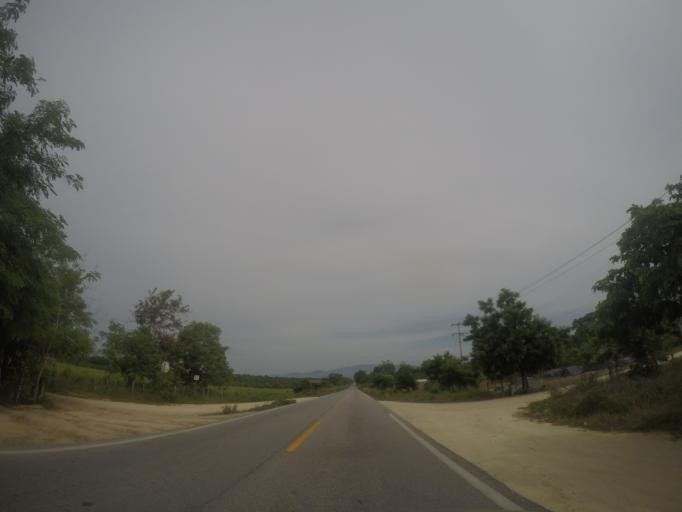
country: MX
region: Oaxaca
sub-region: Villa de Tututepec de Melchor Ocampo
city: Santa Rosa de Lima
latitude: 15.9764
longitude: -97.4037
